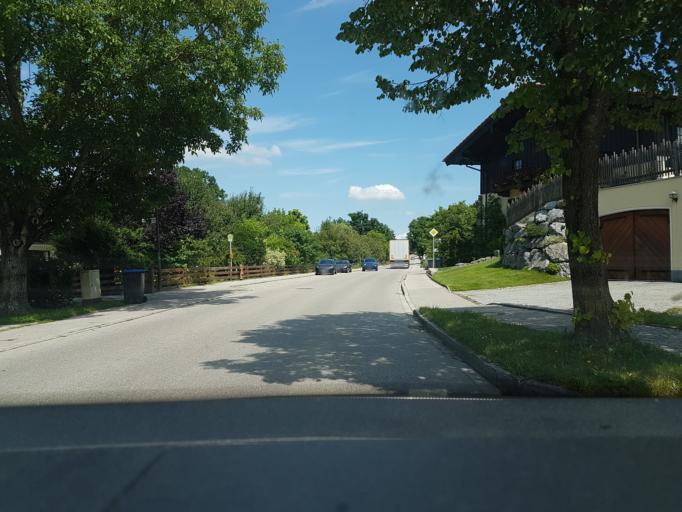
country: DE
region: Bavaria
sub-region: Upper Bavaria
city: Brannenburg
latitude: 47.7658
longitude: 12.0791
